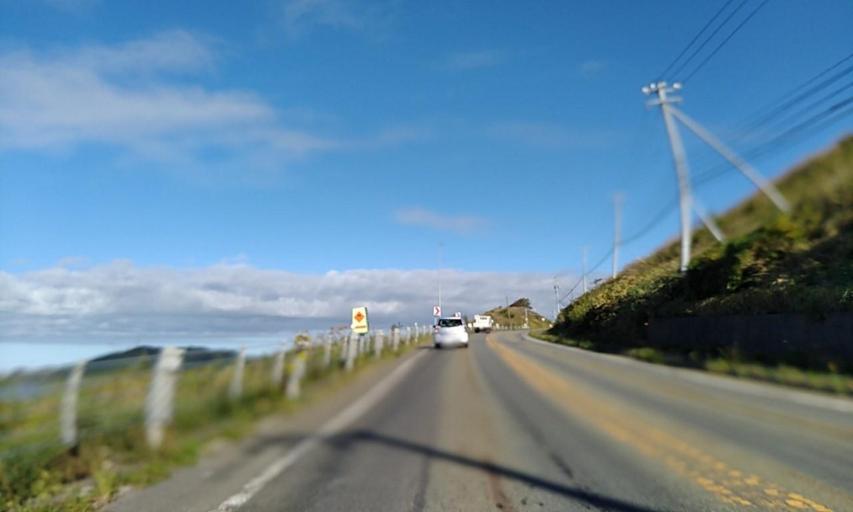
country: JP
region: Hokkaido
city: Shizunai-furukawacho
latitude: 42.1812
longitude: 142.7309
